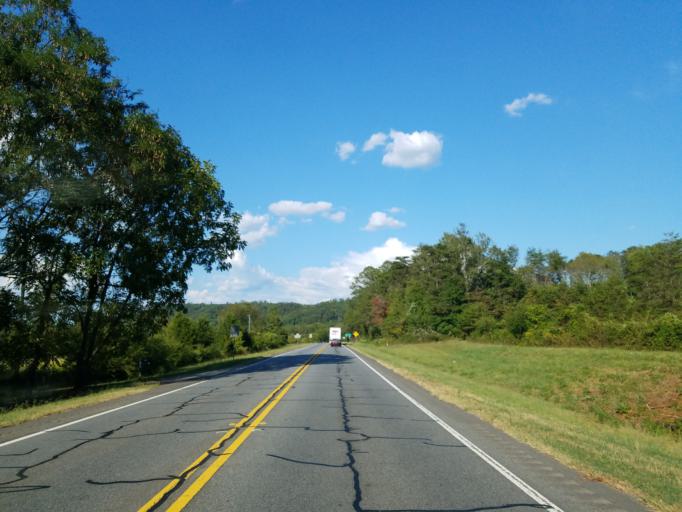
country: US
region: Georgia
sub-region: Bartow County
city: Rydal
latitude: 34.4115
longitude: -84.7003
